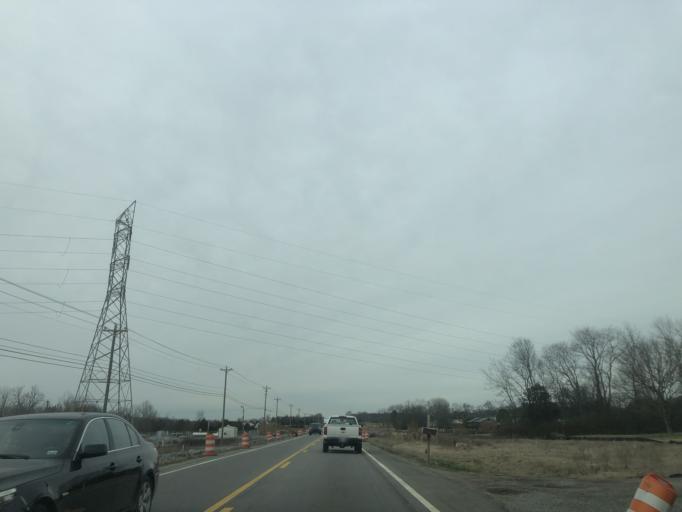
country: US
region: Tennessee
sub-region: Wilson County
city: Mount Juliet
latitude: 36.2462
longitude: -86.4339
